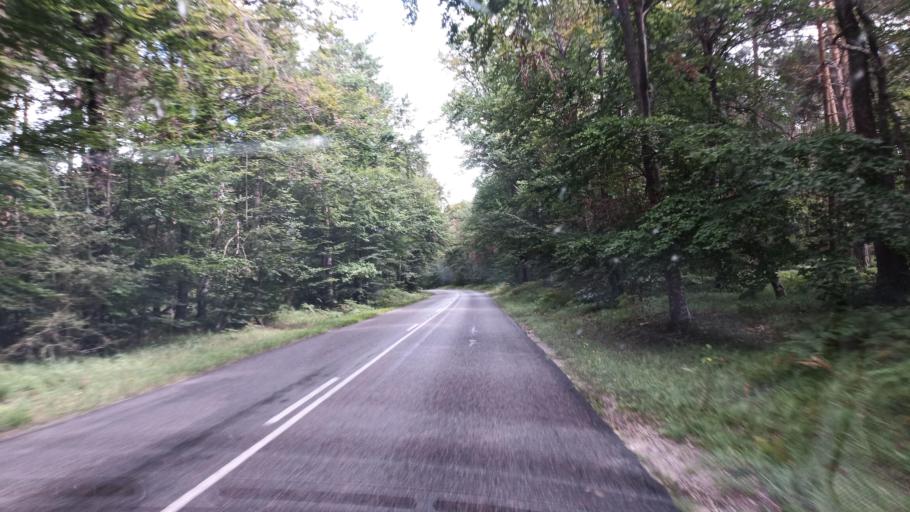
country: FR
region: Ile-de-France
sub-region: Departement de Seine-et-Marne
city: Avon
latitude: 48.3831
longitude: 2.7481
